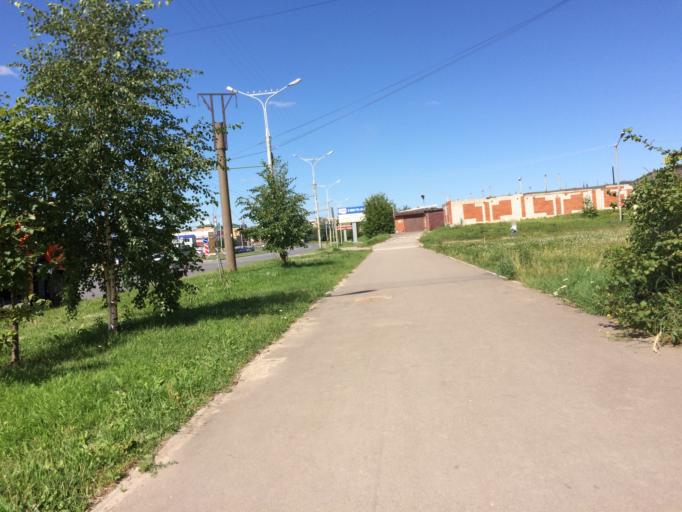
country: RU
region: Mariy-El
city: Yoshkar-Ola
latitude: 56.6249
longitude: 47.9347
